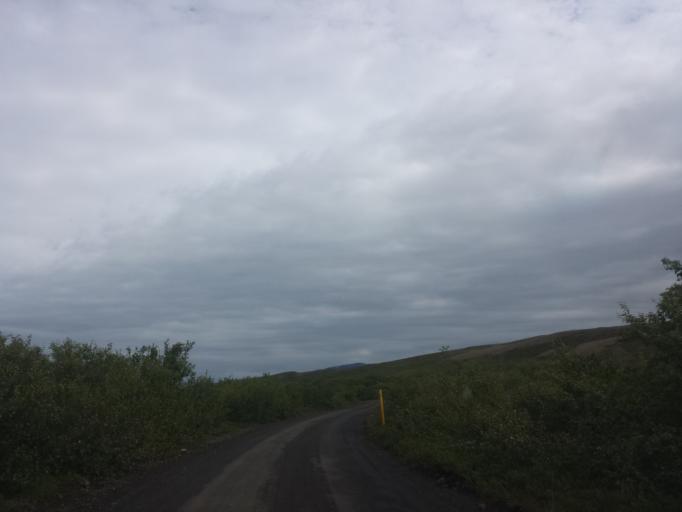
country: IS
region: Northeast
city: Husavik
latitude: 65.9419
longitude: -17.4246
